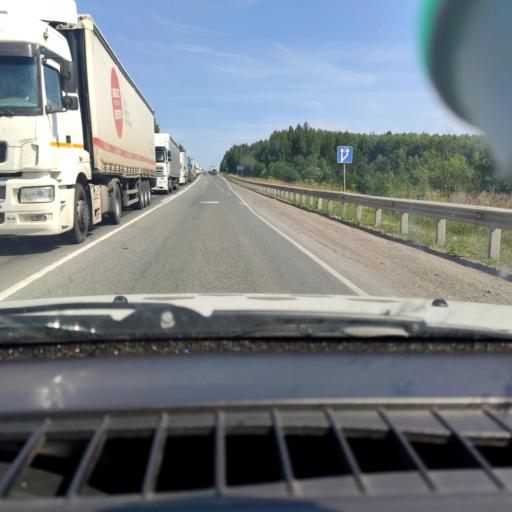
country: RU
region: Perm
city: Nytva
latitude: 57.9816
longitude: 55.2025
